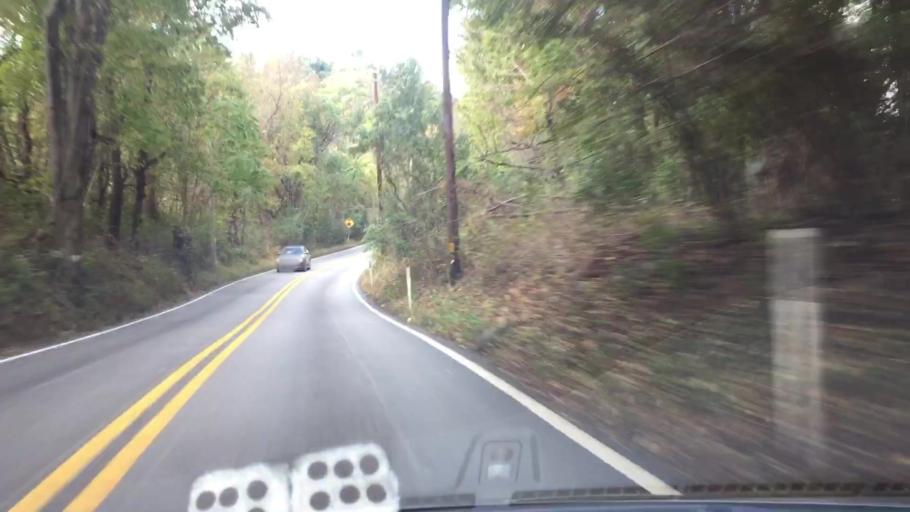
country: US
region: Pennsylvania
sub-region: Delaware County
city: Lima
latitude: 39.9582
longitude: -75.4311
